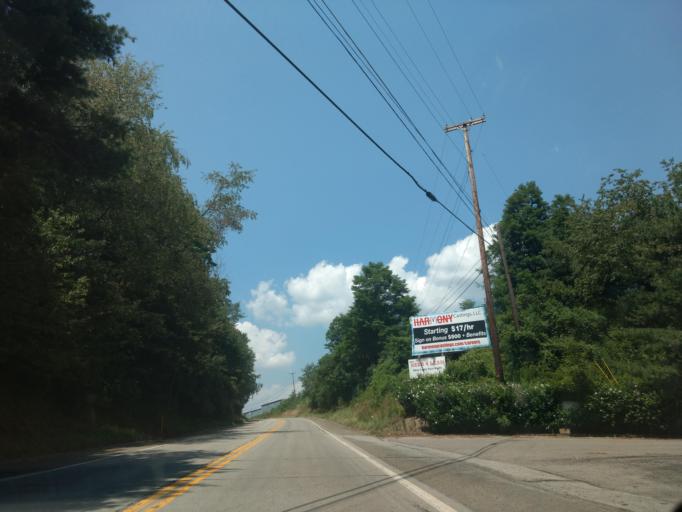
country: US
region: Pennsylvania
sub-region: Butler County
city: Zelienople
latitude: 40.7967
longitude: -80.1066
